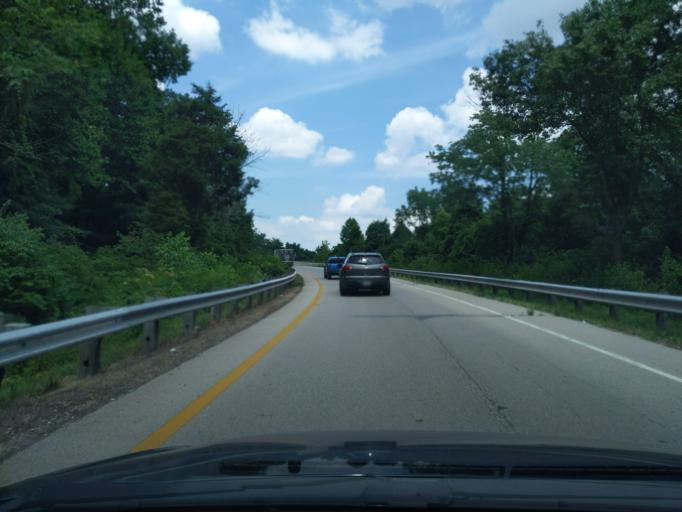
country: US
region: Ohio
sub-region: Hamilton County
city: Highpoint
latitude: 39.2719
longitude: -84.3479
